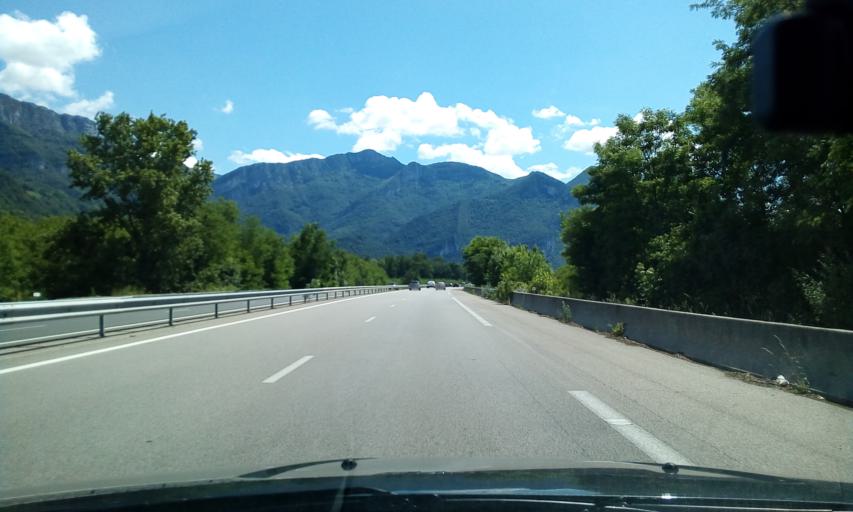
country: FR
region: Rhone-Alpes
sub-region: Departement de l'Isere
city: Tullins
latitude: 45.2250
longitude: 5.4811
